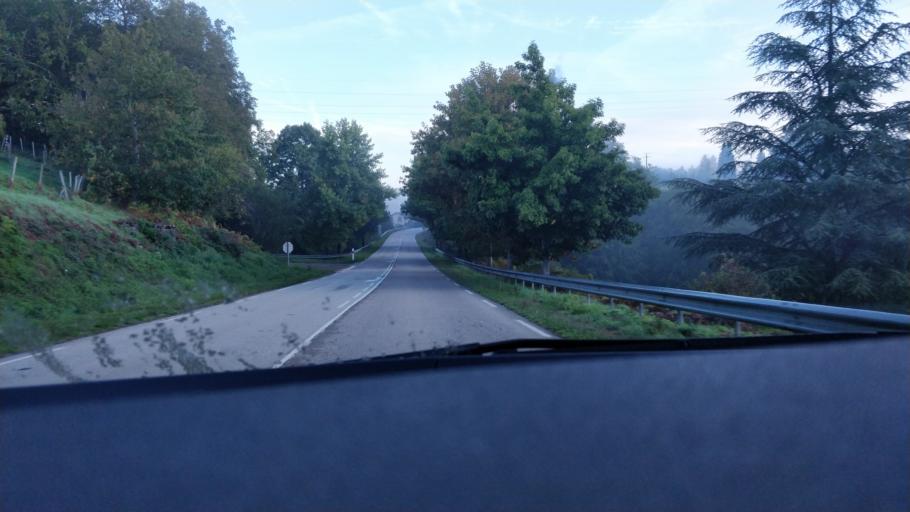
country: FR
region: Limousin
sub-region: Departement de la Haute-Vienne
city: Saint-Leonard-de-Noblat
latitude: 45.8470
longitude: 1.4941
